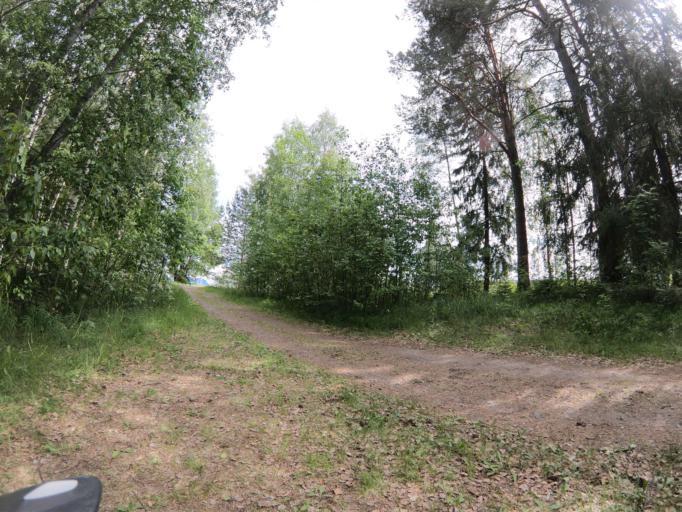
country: SE
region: Vaesterbotten
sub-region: Umea Kommun
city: Umea
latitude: 63.8205
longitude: 20.2250
